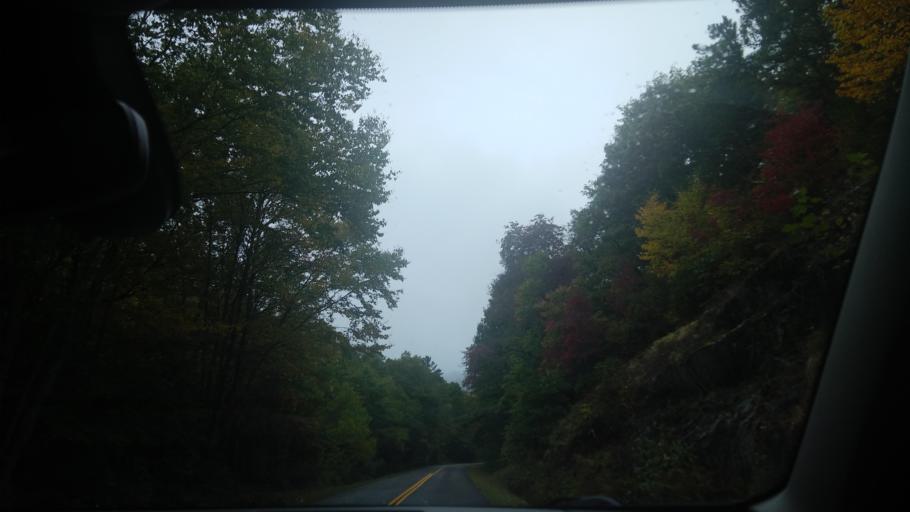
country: US
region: North Carolina
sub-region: Mitchell County
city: Spruce Pine
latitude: 35.9064
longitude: -81.9672
